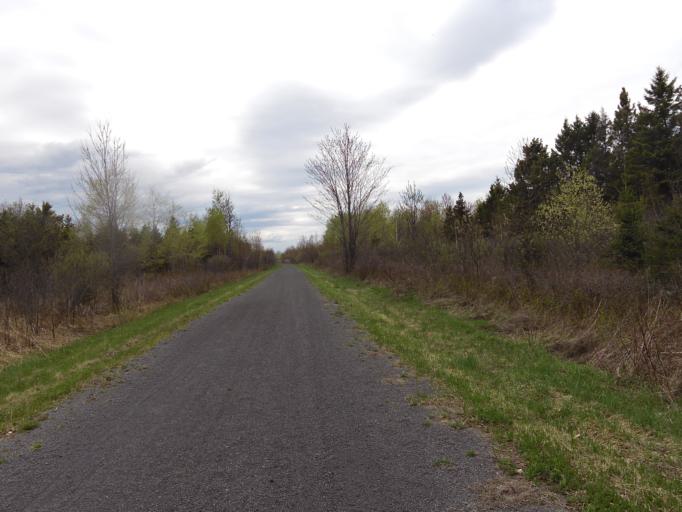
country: CA
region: Ontario
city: Hawkesbury
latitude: 45.5444
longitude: -74.7723
